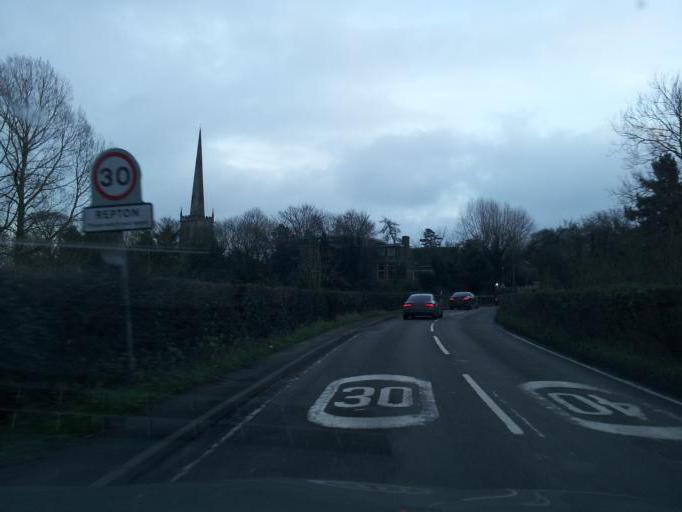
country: GB
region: England
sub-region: Derbyshire
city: Repton
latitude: 52.8421
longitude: -1.5546
